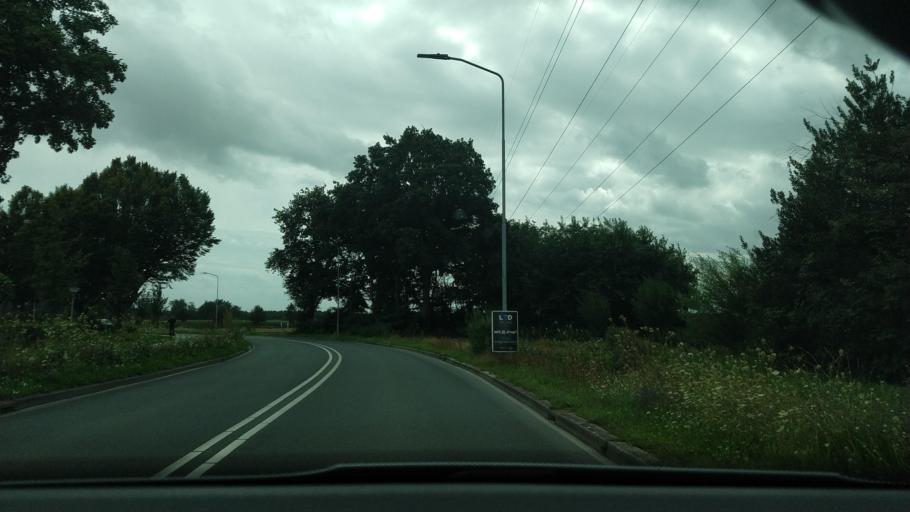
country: NL
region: Gelderland
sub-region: Gemeente Ermelo
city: Horst
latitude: 52.2992
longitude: 5.5966
